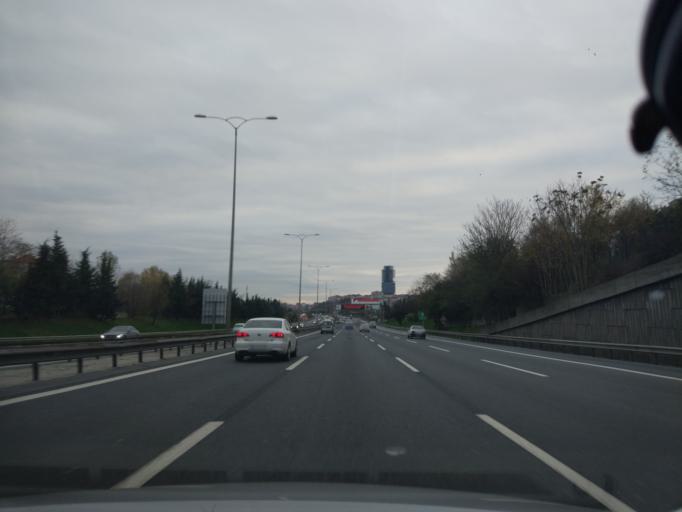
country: TR
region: Istanbul
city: Sisli
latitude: 41.0956
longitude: 29.0187
